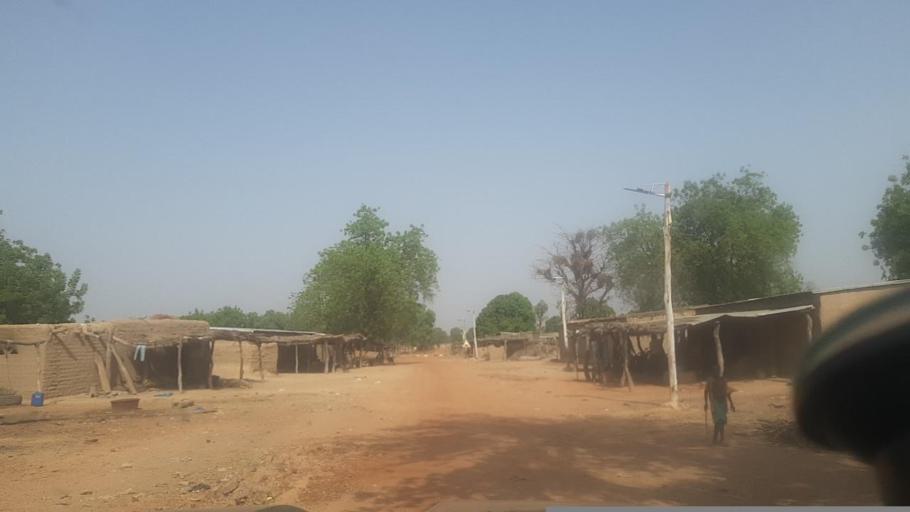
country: ML
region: Segou
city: Bla
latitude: 12.8473
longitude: -5.9918
